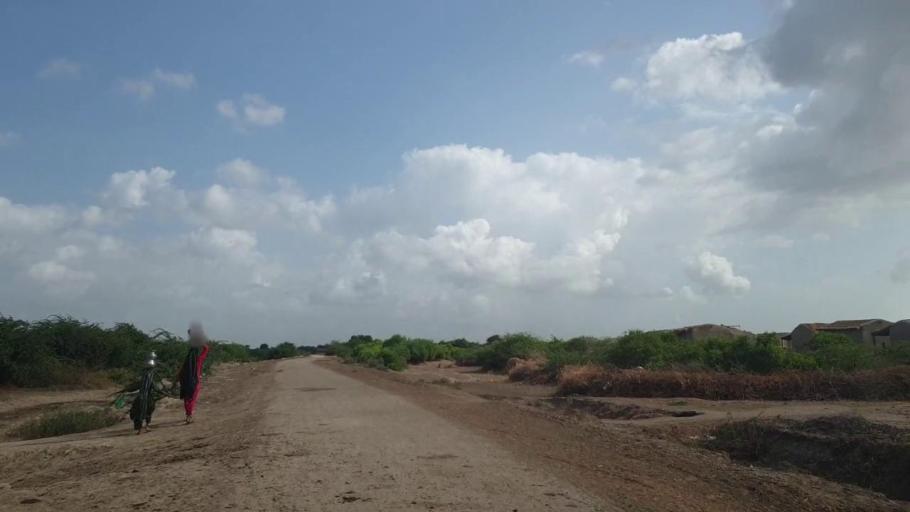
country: PK
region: Sindh
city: Kadhan
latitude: 24.5528
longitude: 69.0636
